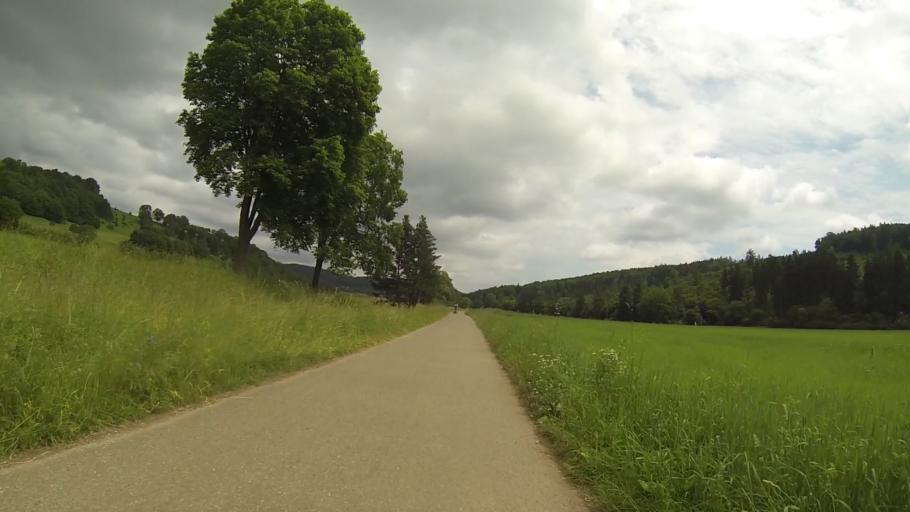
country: DE
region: Baden-Wuerttemberg
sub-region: Regierungsbezirk Stuttgart
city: Steinheim am Albuch
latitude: 48.6755
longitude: 10.0817
